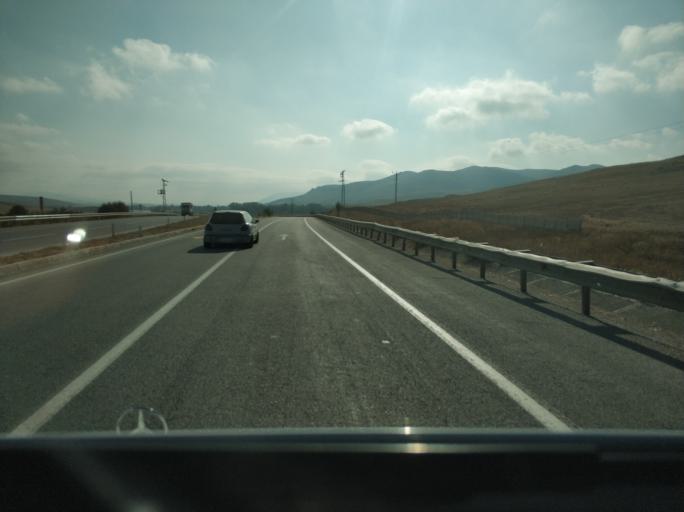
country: TR
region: Sivas
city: Yildizeli
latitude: 39.8359
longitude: 36.4435
